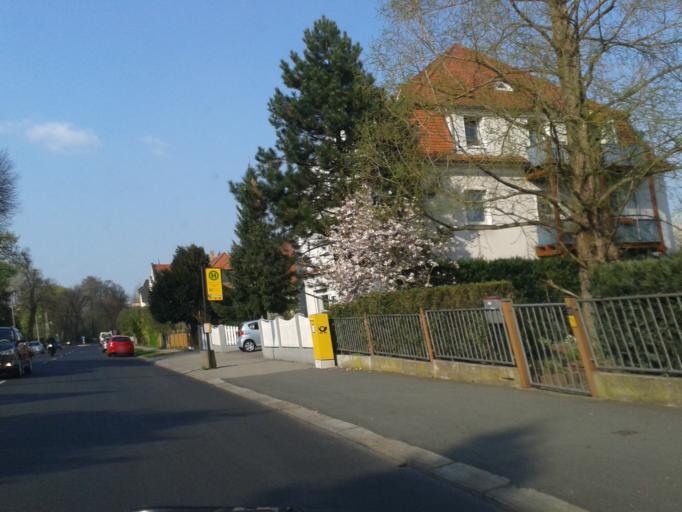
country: DE
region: Saxony
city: Dresden
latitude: 51.0158
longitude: 13.7556
